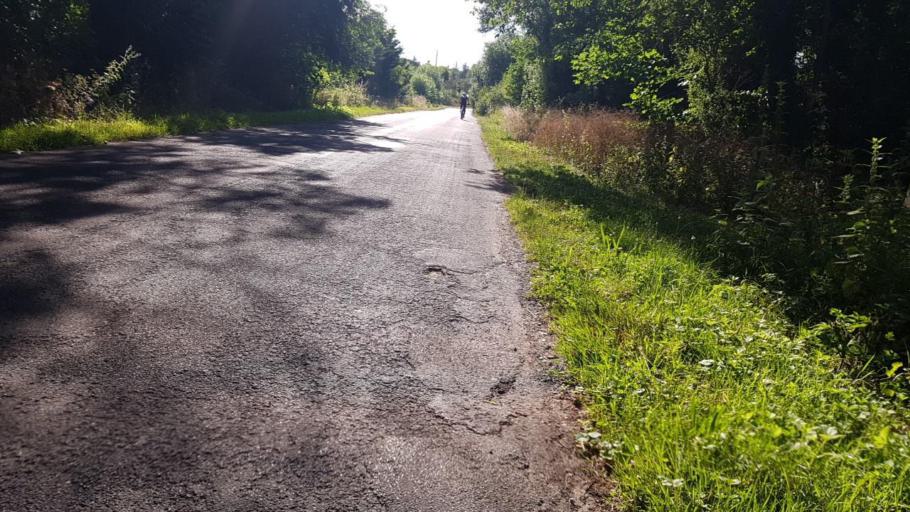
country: FR
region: Picardie
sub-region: Departement de l'Oise
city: Senlis
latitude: 49.1970
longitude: 2.6008
